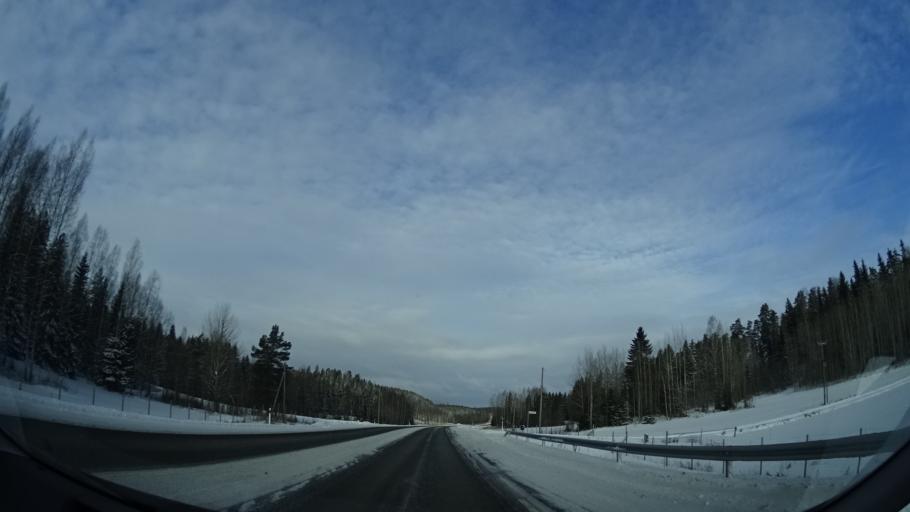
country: FI
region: Uusimaa
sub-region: Helsinki
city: Karkkila
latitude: 60.5774
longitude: 24.1392
